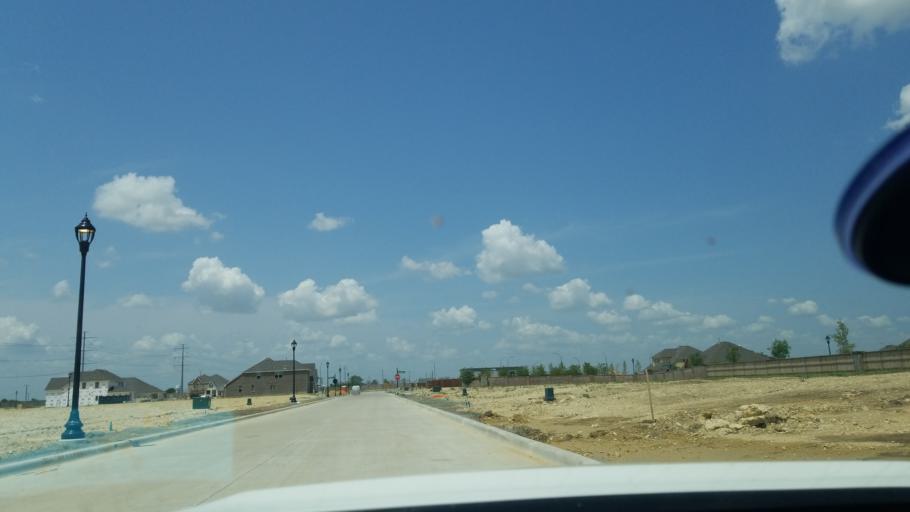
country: US
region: Texas
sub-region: Tarrant County
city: Haslet
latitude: 32.9414
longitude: -97.3978
